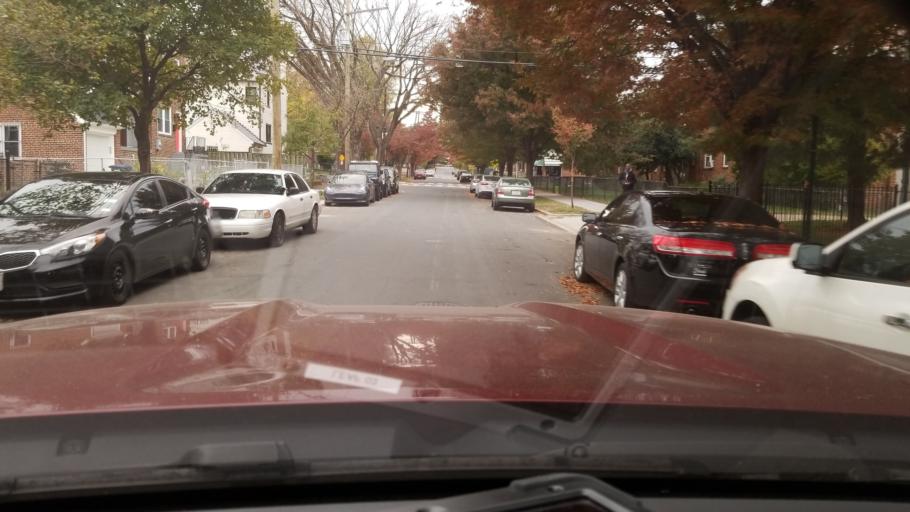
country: US
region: Maryland
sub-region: Prince George's County
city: Hillcrest Heights
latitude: 38.8715
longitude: -76.9774
